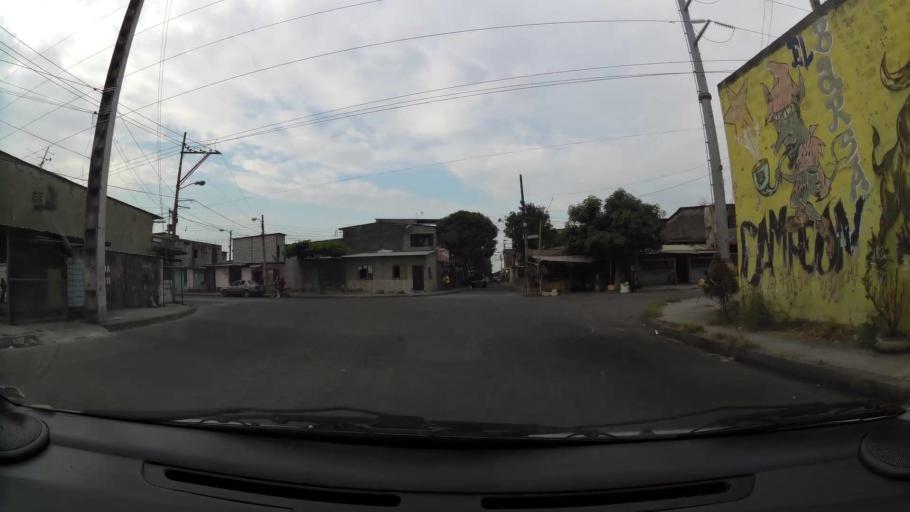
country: EC
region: Guayas
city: Guayaquil
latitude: -2.2563
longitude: -79.8711
